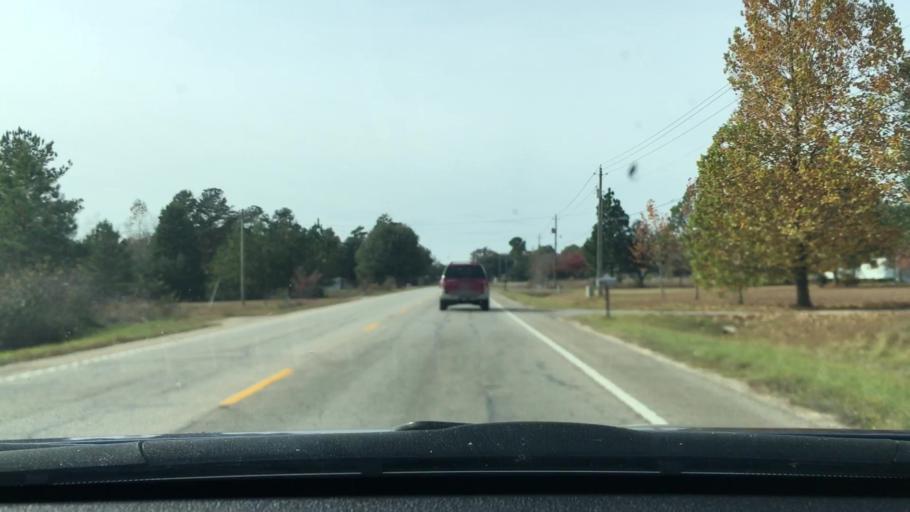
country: US
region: South Carolina
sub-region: Sumter County
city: Cherryvale
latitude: 33.9373
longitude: -80.4654
